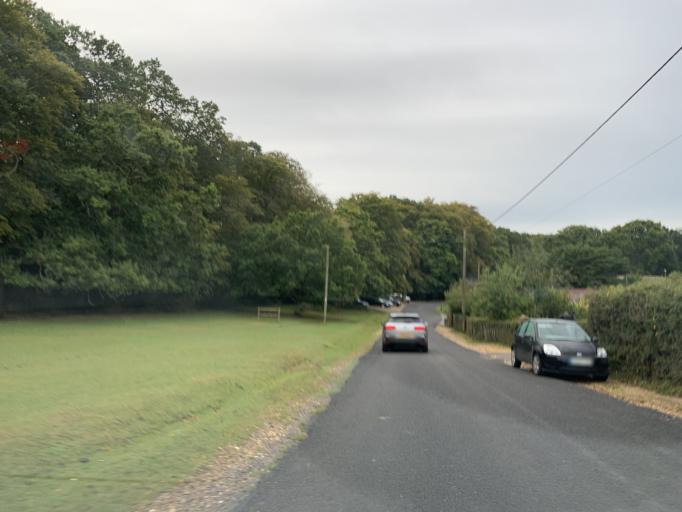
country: GB
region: England
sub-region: Wiltshire
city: Whiteparish
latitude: 50.9536
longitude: -1.6410
